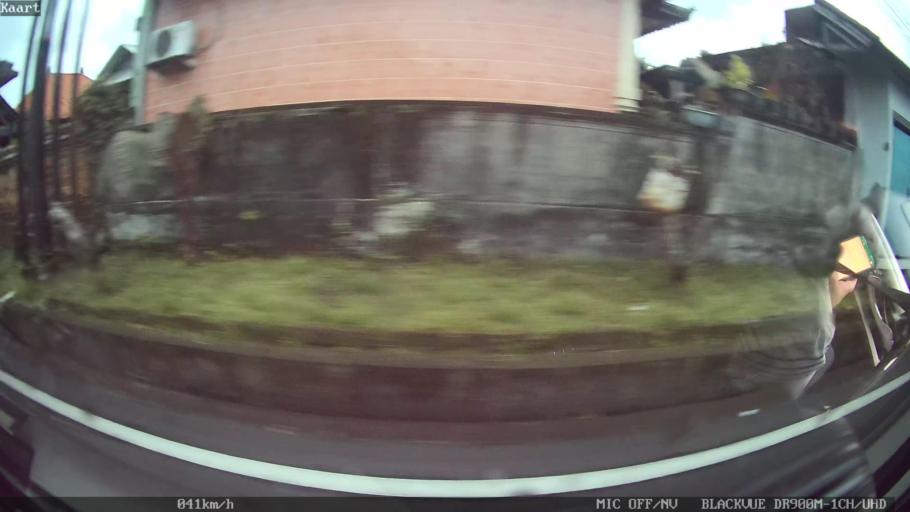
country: ID
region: Bali
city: Banjar Sayanbaleran
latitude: -8.5215
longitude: 115.1868
